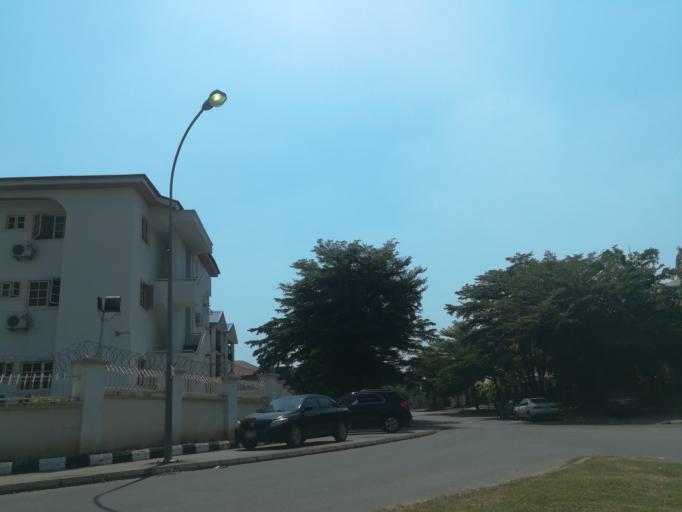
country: NG
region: Abuja Federal Capital Territory
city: Abuja
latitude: 9.0735
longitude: 7.4424
